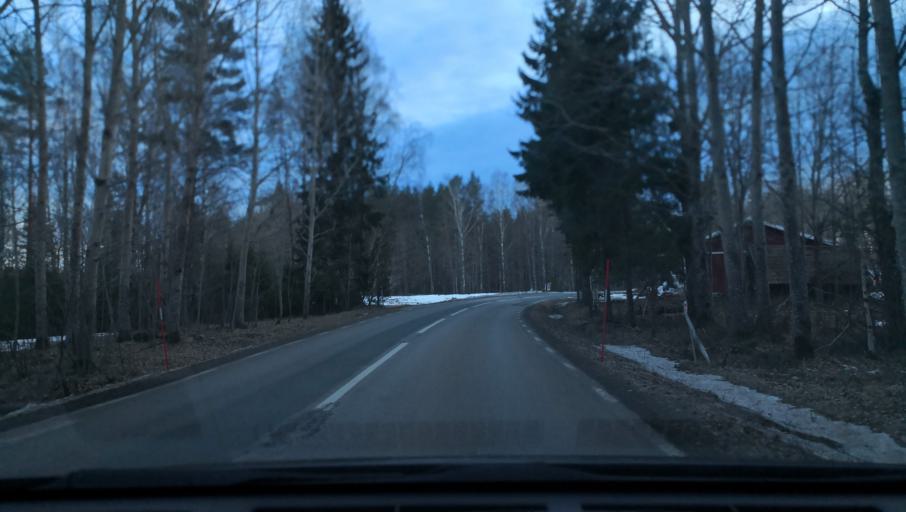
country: SE
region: Uppsala
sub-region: Osthammars Kommun
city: Osterbybruk
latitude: 60.2748
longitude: 17.9601
